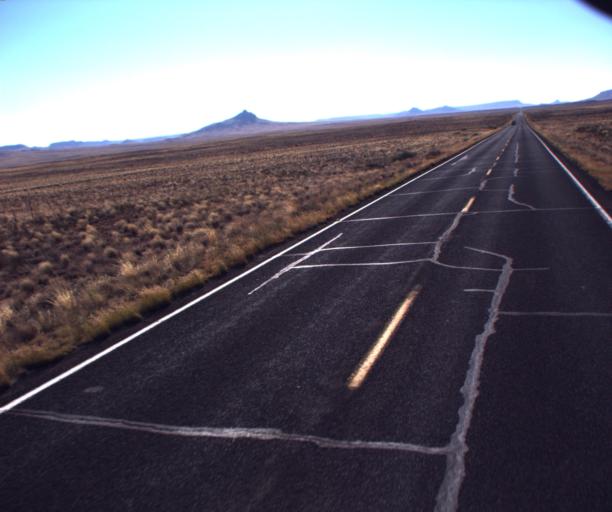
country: US
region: Arizona
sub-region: Navajo County
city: Dilkon
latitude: 35.5947
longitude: -110.4689
